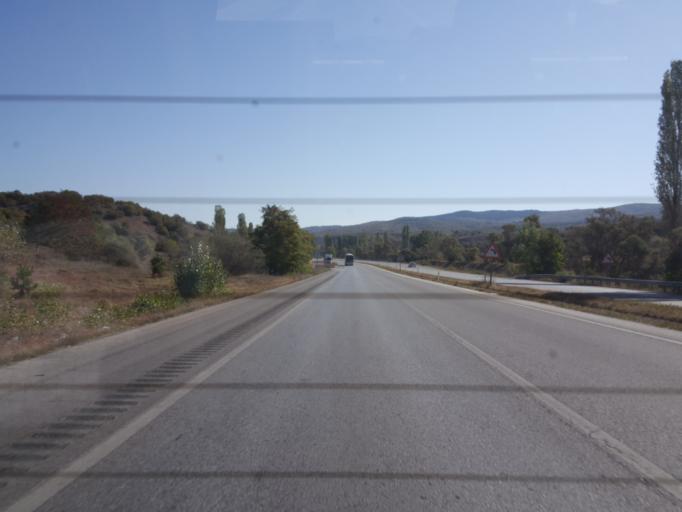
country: TR
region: Corum
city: Alaca
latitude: 40.3179
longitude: 34.6831
